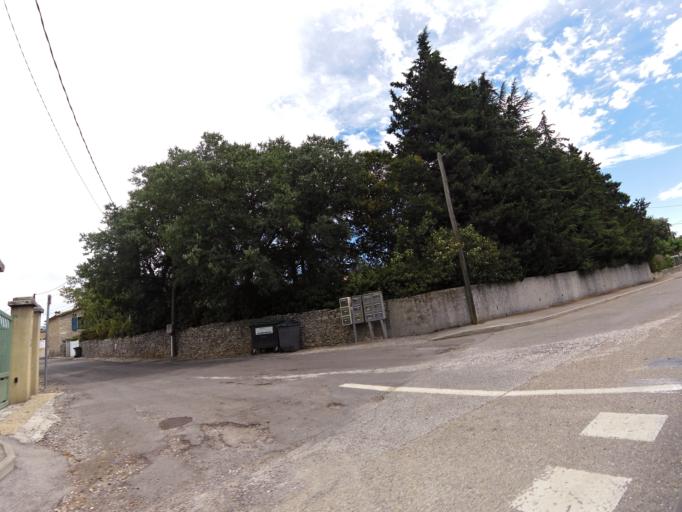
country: FR
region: Languedoc-Roussillon
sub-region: Departement du Gard
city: Quissac
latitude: 43.9132
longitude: 3.9962
